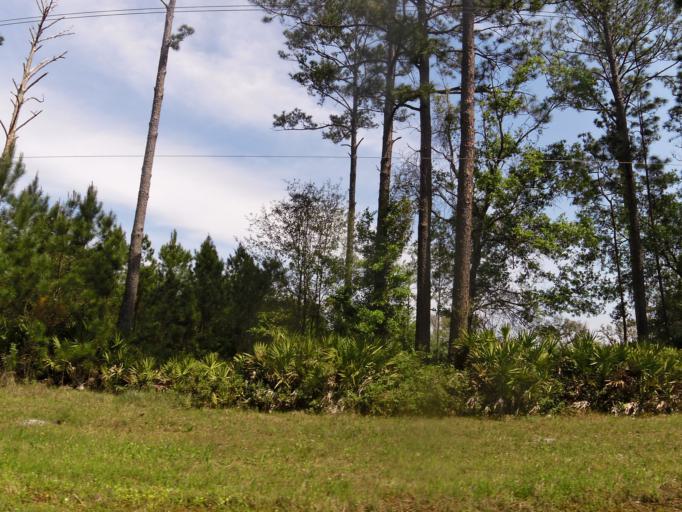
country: US
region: Florida
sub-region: Nassau County
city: Yulee
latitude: 30.5125
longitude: -81.6603
